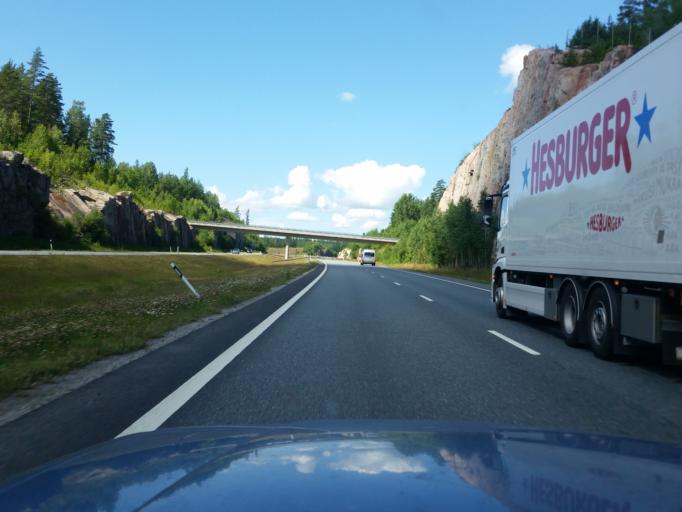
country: FI
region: Varsinais-Suomi
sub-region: Salo
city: Pertteli
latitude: 60.3983
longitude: 23.2480
